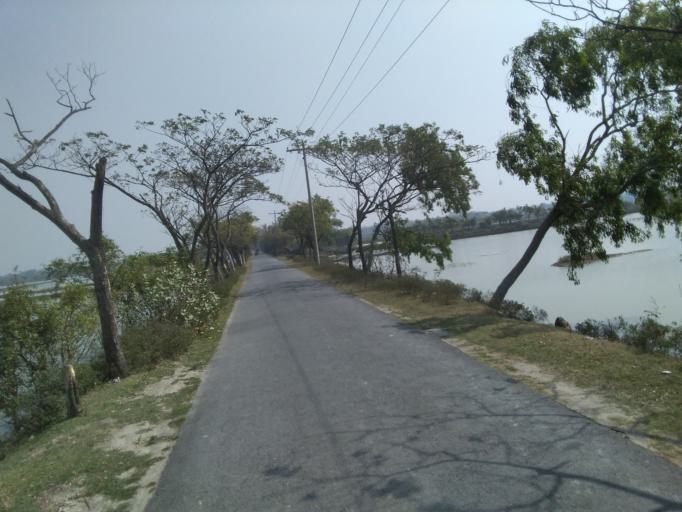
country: IN
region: West Bengal
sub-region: North 24 Parganas
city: Taki
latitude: 22.5936
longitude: 88.9849
